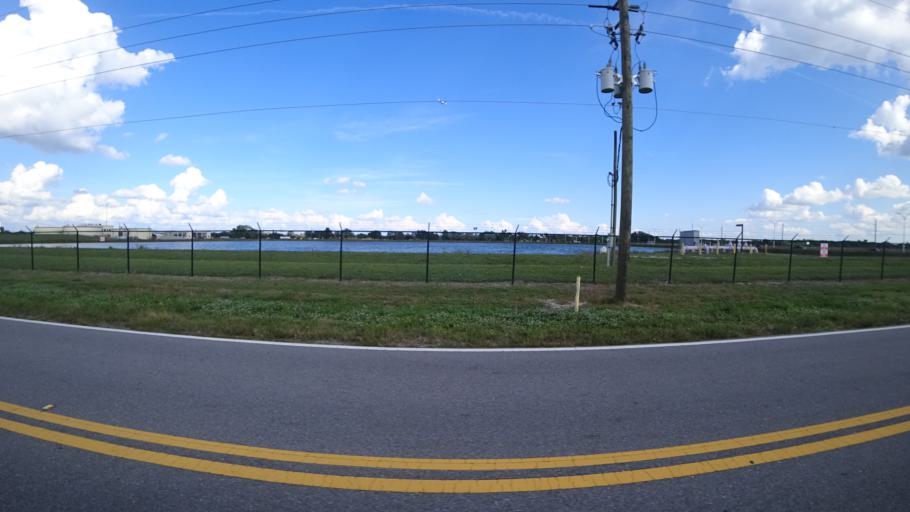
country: US
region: Florida
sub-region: Manatee County
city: Bayshore Gardens
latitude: 27.4492
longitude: -82.6285
